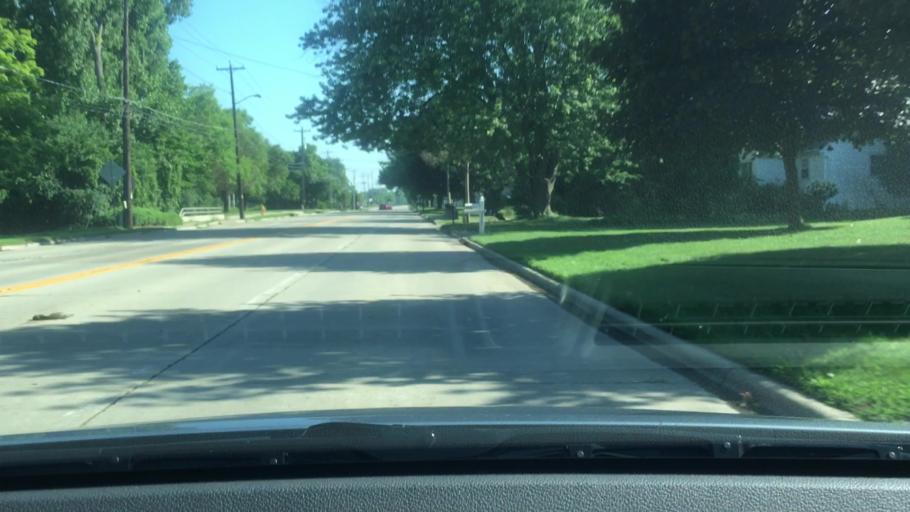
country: US
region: Wisconsin
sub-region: Winnebago County
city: Oshkosh
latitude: 43.9904
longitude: -88.5426
